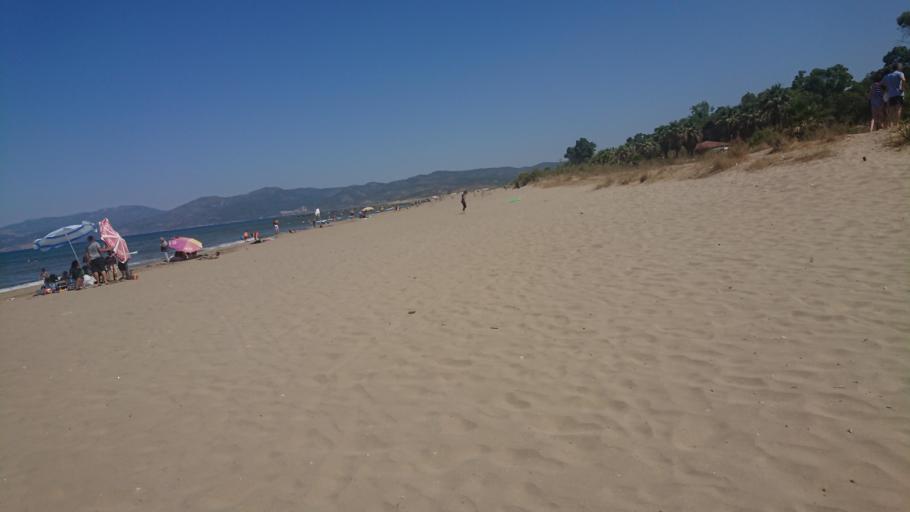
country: TR
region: Aydin
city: Kusadasi
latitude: 37.9373
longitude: 27.2758
